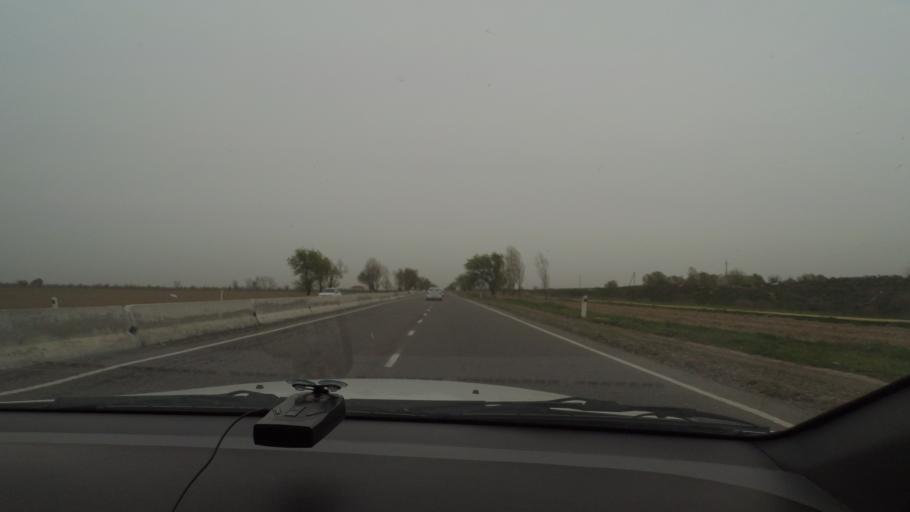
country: UZ
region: Jizzax
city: Gagarin
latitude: 40.5309
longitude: 68.3419
